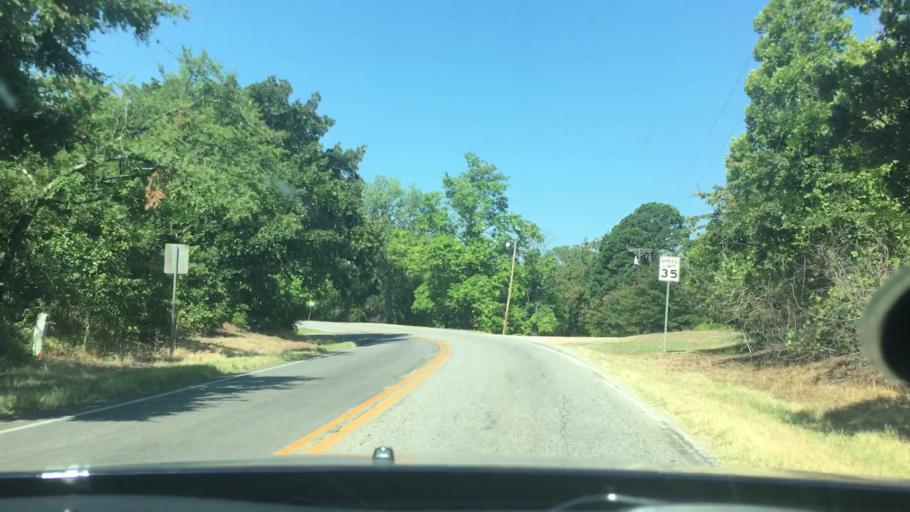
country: US
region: Oklahoma
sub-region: Johnston County
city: Tishomingo
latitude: 34.2405
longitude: -96.5543
